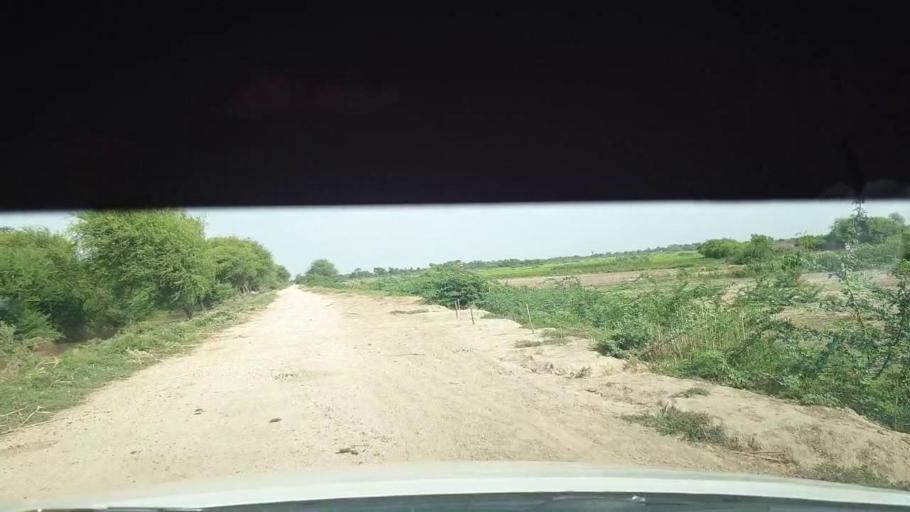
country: PK
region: Sindh
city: Kadhan
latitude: 24.5191
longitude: 69.0049
